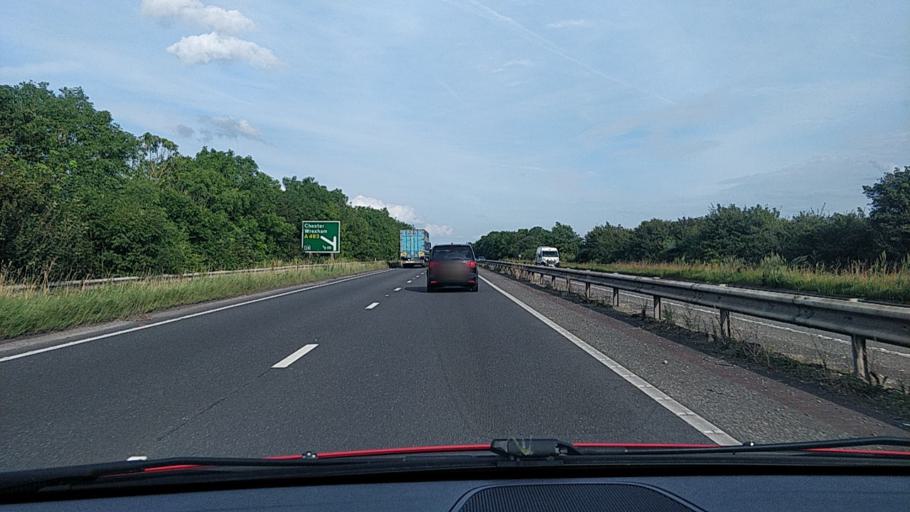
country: GB
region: England
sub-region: Cheshire West and Chester
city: Eccleston
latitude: 53.1573
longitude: -2.9319
